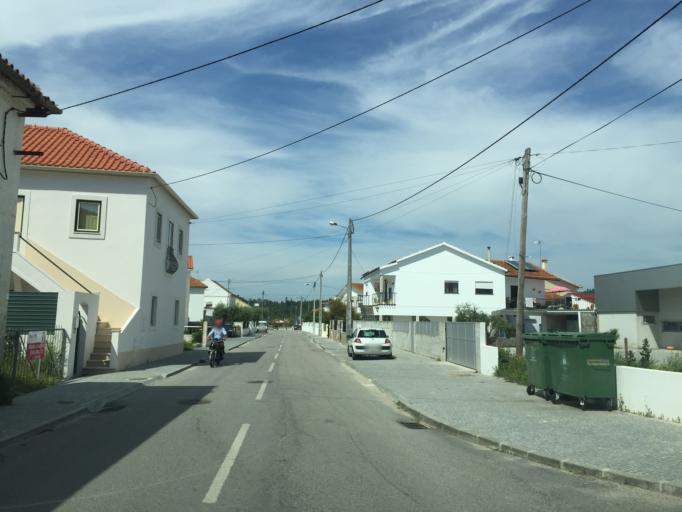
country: PT
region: Coimbra
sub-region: Soure
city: Soure
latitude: 40.0059
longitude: -8.5810
